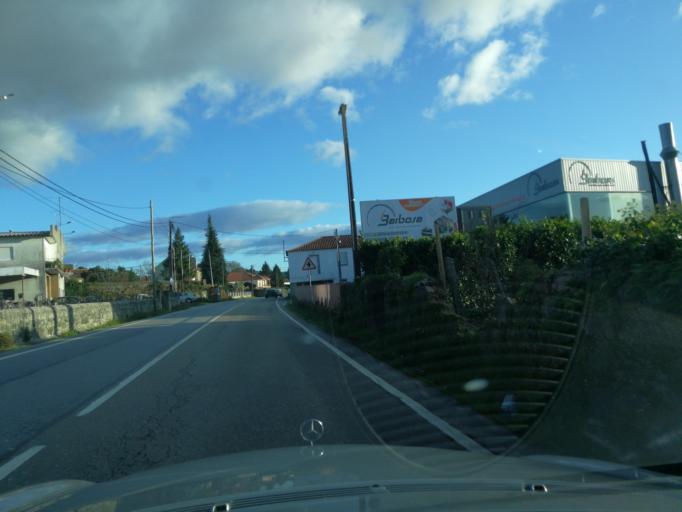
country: PT
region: Braga
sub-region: Esposende
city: Marinhas
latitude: 41.6134
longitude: -8.7430
